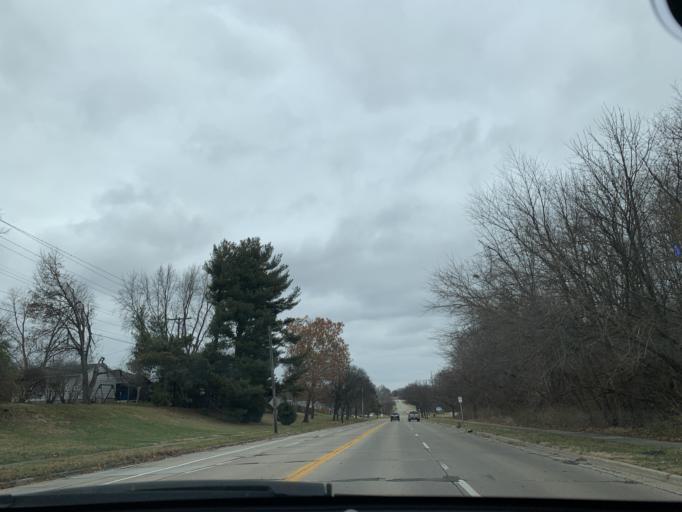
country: US
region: Illinois
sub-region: Sangamon County
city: Leland Grove
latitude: 39.8170
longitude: -89.6872
